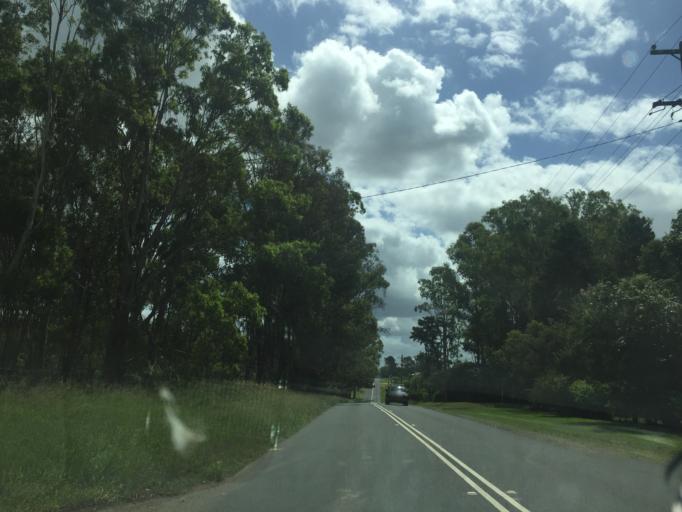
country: AU
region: New South Wales
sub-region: Penrith Municipality
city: Kingswood Park
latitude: -33.7961
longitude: 150.7157
